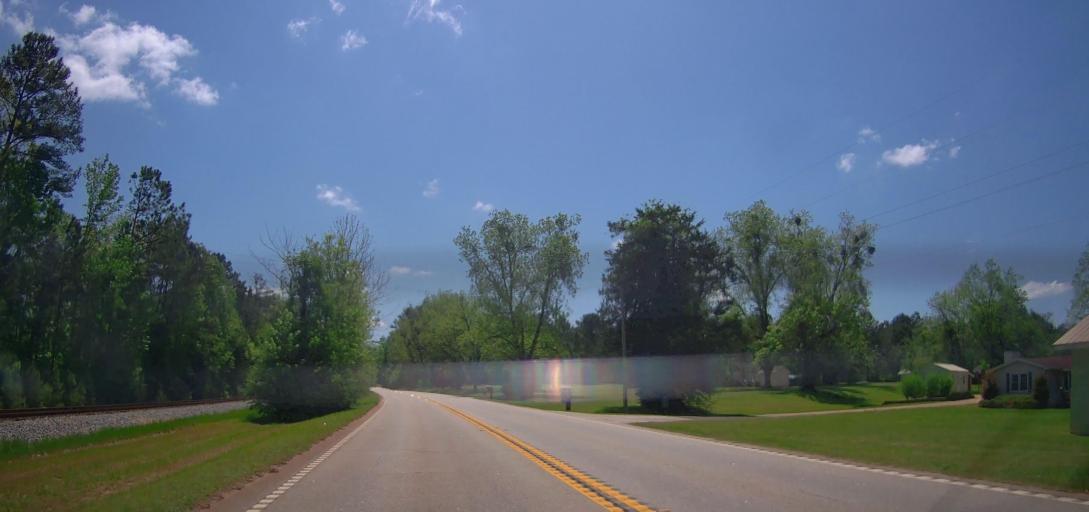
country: US
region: Georgia
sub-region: Jasper County
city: Monticello
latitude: 33.2281
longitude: -83.6749
